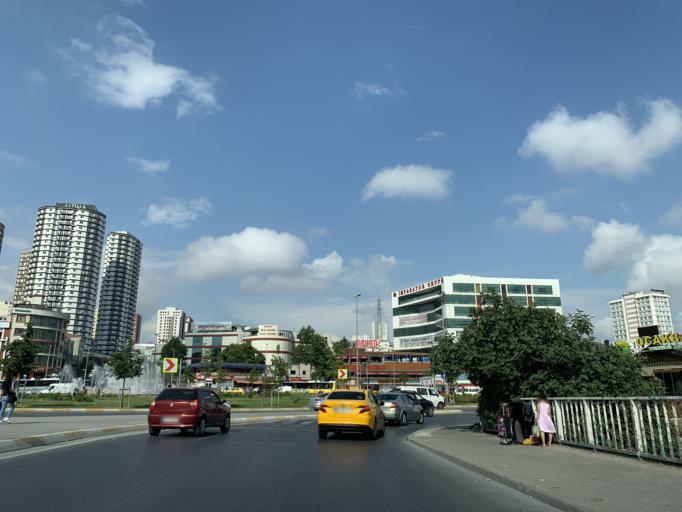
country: TR
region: Istanbul
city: Esenyurt
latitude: 41.0280
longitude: 28.6657
